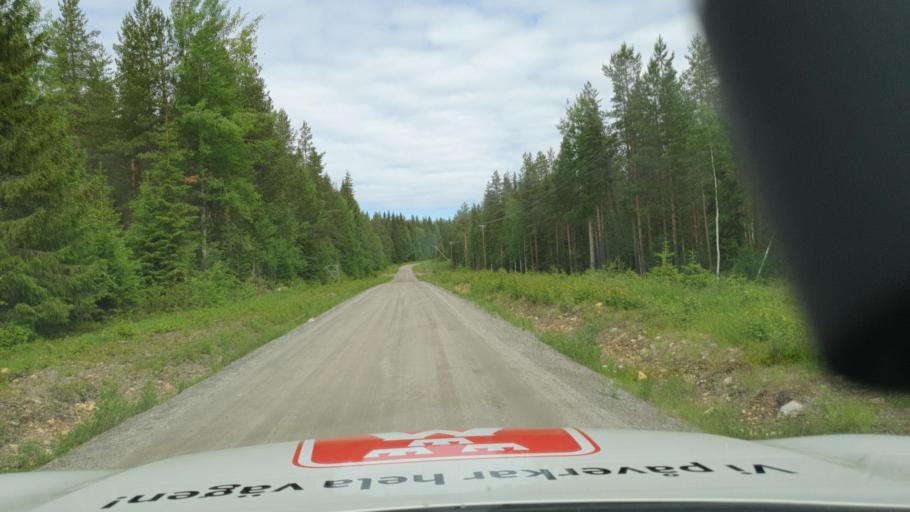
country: SE
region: Vaesterbotten
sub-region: Skelleftea Kommun
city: Langsele
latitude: 64.5503
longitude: 20.2846
